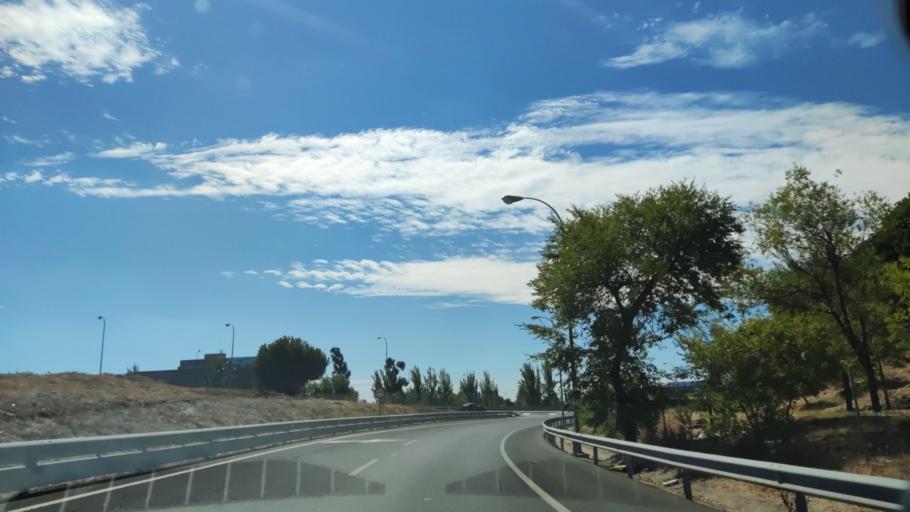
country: ES
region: Madrid
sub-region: Provincia de Madrid
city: Puente de Vallecas
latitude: 40.3911
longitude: -3.6322
